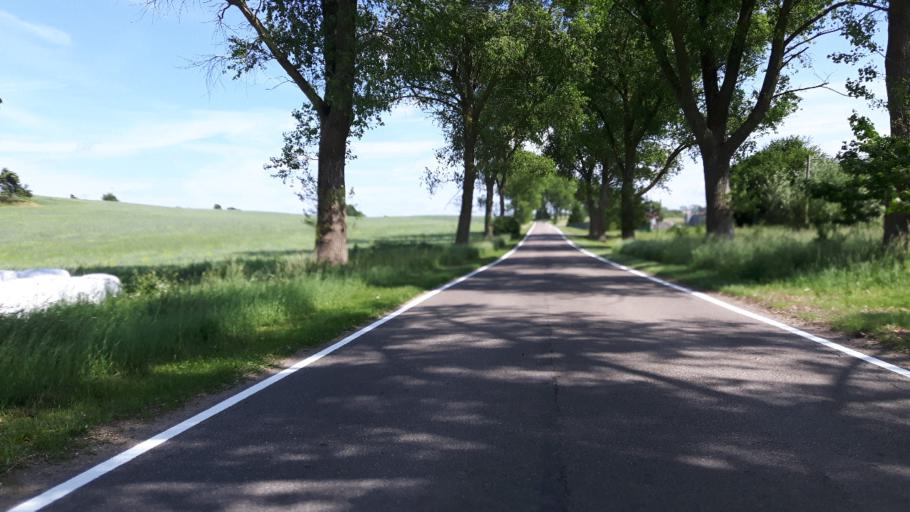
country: PL
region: Pomeranian Voivodeship
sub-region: Powiat wejherowski
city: Gniewino
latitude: 54.7205
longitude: 17.9894
